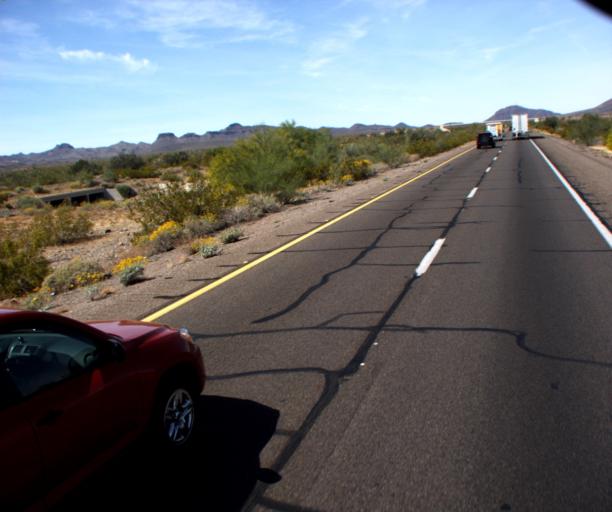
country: US
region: Arizona
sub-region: La Paz County
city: Quartzsite
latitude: 33.6557
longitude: -113.9578
